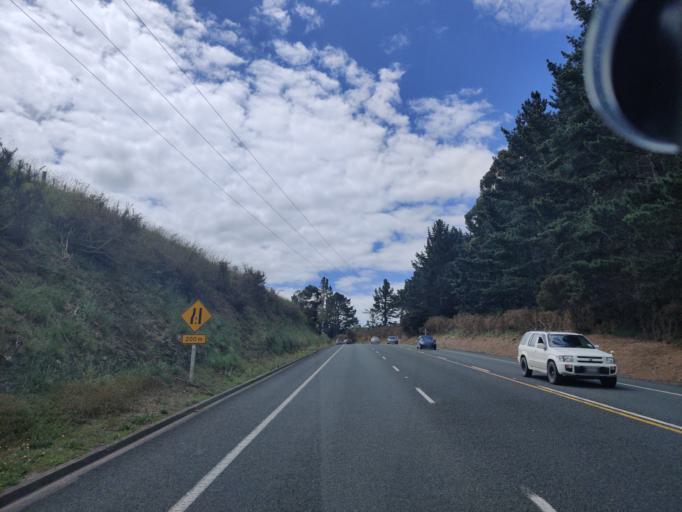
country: NZ
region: Northland
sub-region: Far North District
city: Kerikeri
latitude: -35.2839
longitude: 173.9562
